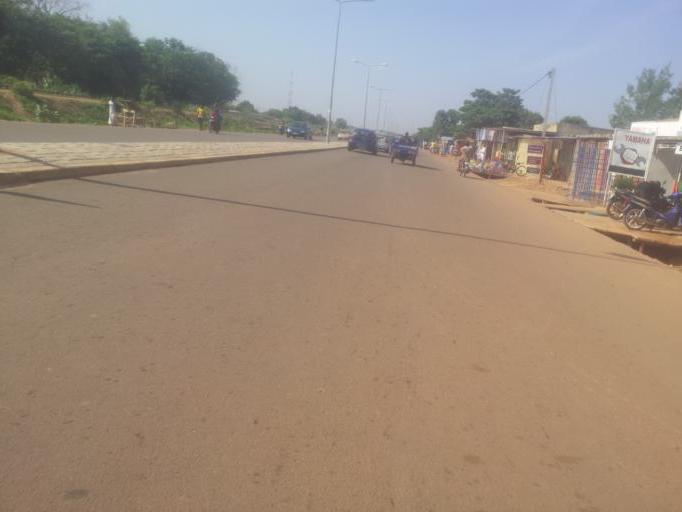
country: BF
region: Centre
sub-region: Kadiogo Province
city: Ouagadougou
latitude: 12.3790
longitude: -1.5701
